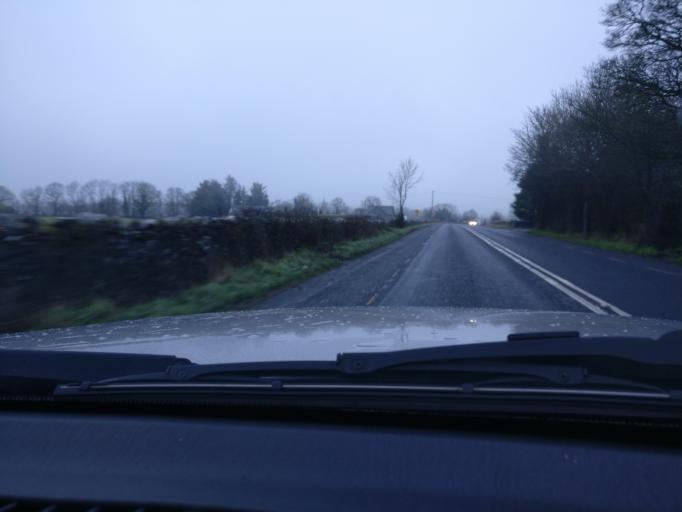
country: IE
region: Connaught
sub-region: County Galway
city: Loughrea
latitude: 53.2558
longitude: -8.4393
